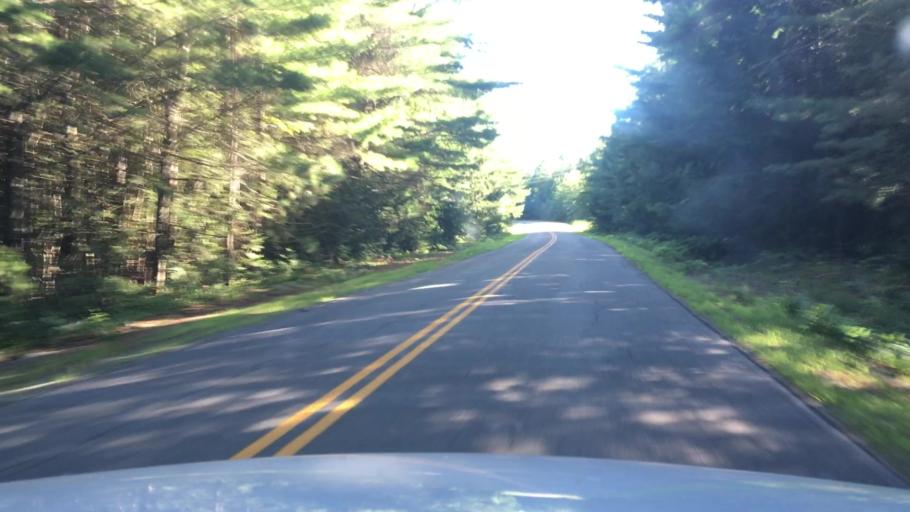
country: US
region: Maine
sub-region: Penobscot County
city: Enfield
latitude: 45.2110
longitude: -68.5897
